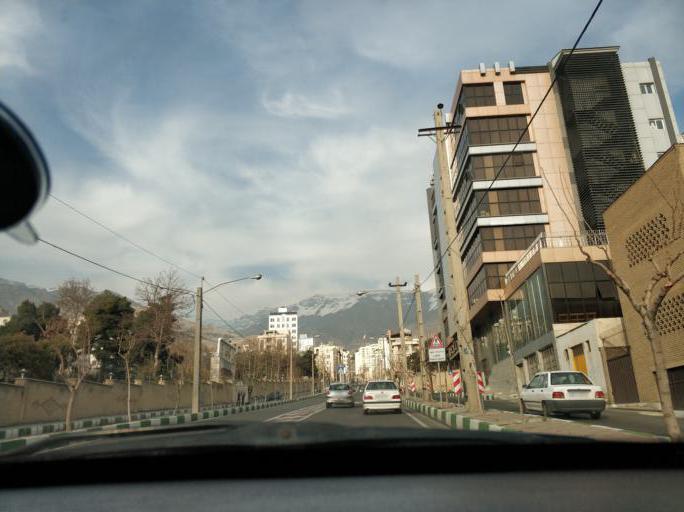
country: IR
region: Tehran
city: Tajrish
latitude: 35.8051
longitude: 51.4823
